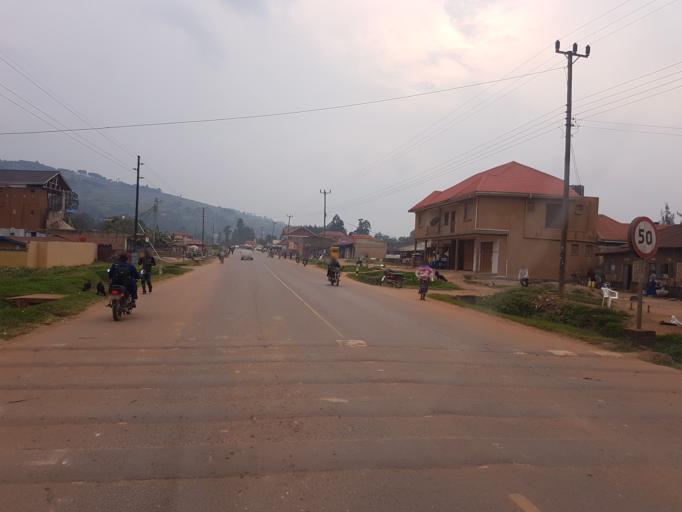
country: UG
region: Western Region
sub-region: Kabale District
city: Kabale
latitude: -1.2463
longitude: 29.9781
